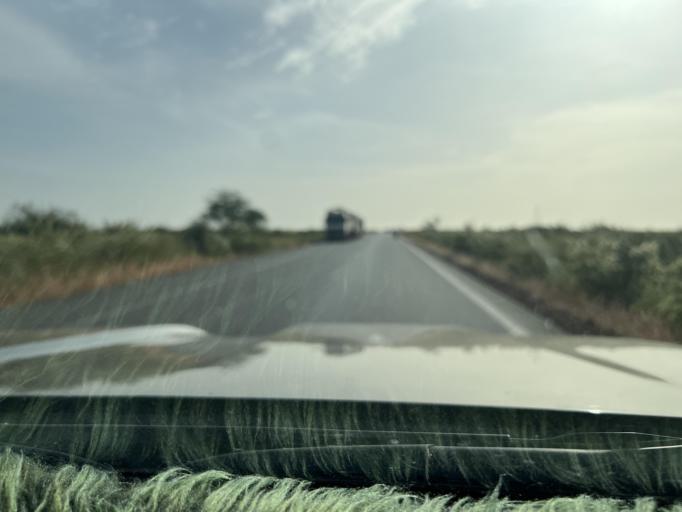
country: ML
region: Segou
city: Baroueli
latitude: 12.9535
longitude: -6.7289
